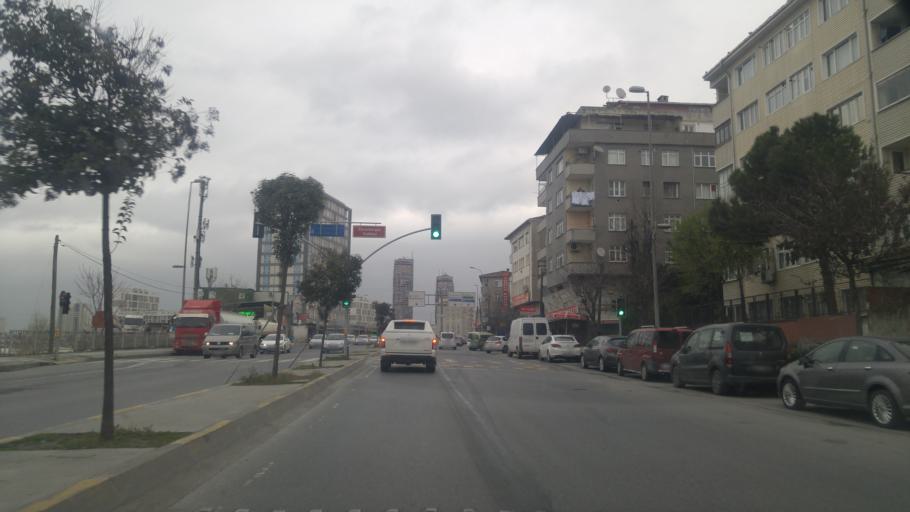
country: TR
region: Istanbul
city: Mahmutbey
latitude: 41.0311
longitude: 28.7682
